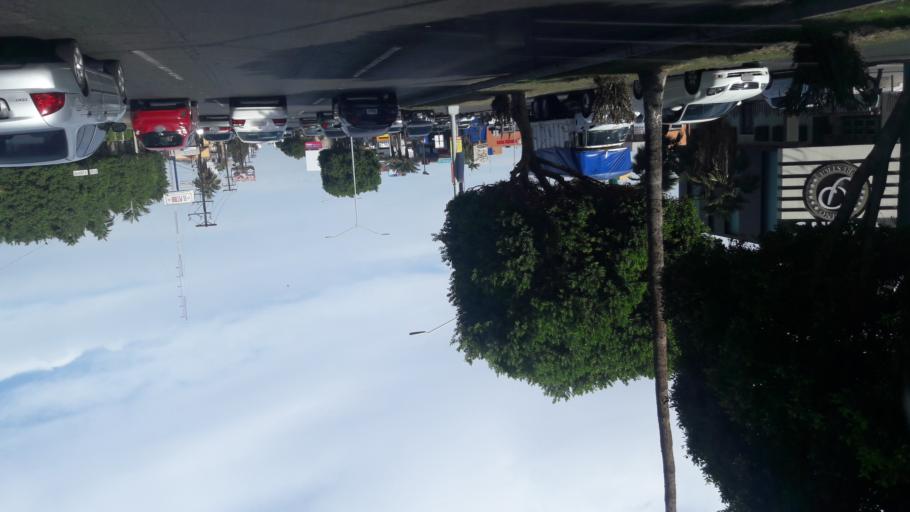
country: MX
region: Baja California
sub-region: Mexicali
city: Mexicali
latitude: 32.6388
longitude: -115.4490
